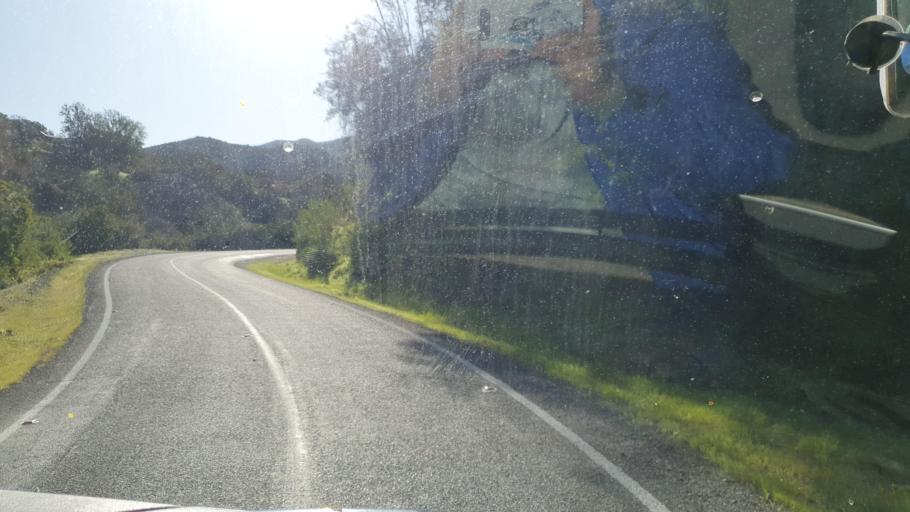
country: CL
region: Valparaiso
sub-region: Provincia de Marga Marga
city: Limache
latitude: -33.1807
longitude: -71.1792
